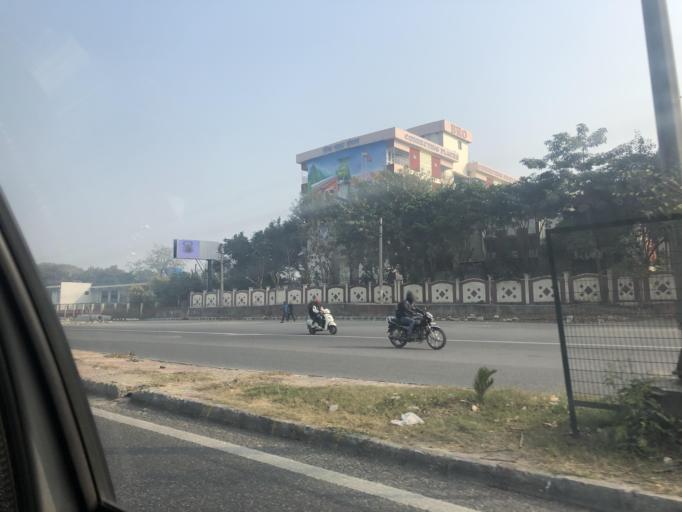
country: IN
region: NCT
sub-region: Central Delhi
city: Karol Bagh
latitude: 28.6148
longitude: 77.1364
